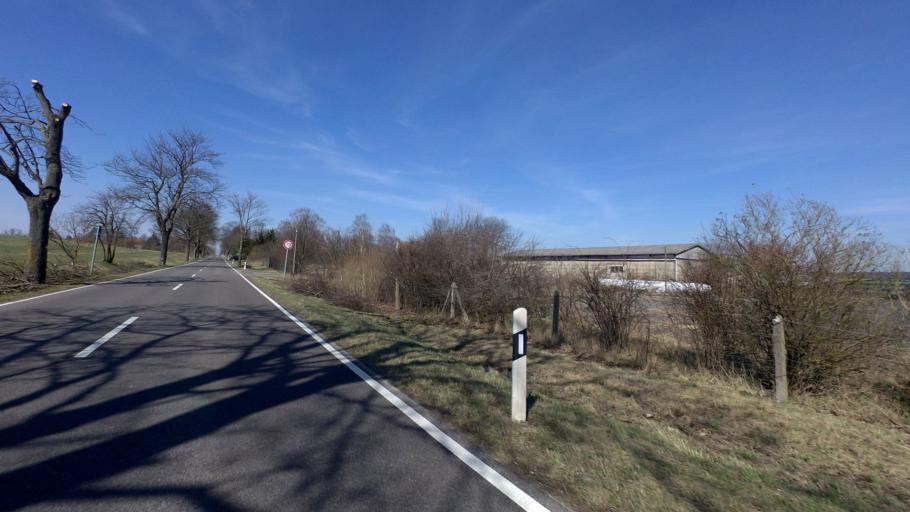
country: DE
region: Brandenburg
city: Buckow
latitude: 52.5943
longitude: 14.0265
